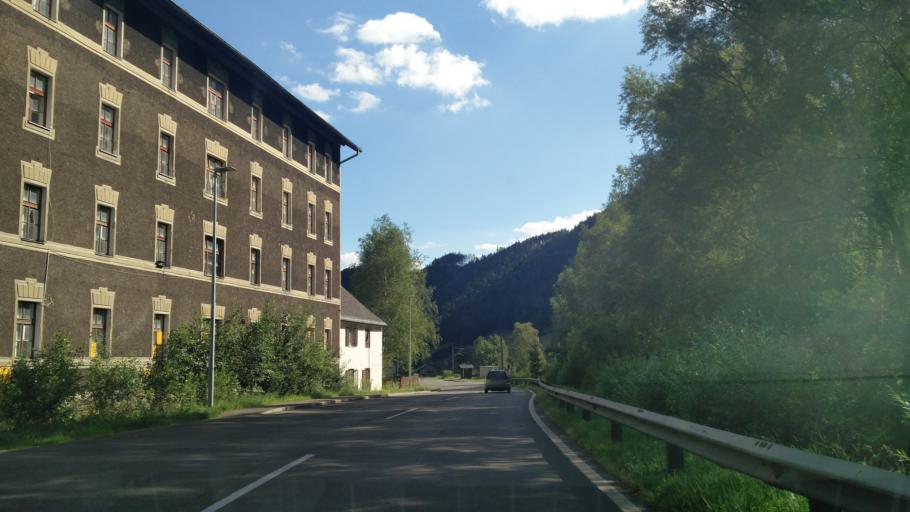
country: AT
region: Styria
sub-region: Politischer Bezirk Leoben
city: Vordernberg
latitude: 47.4766
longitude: 14.9881
